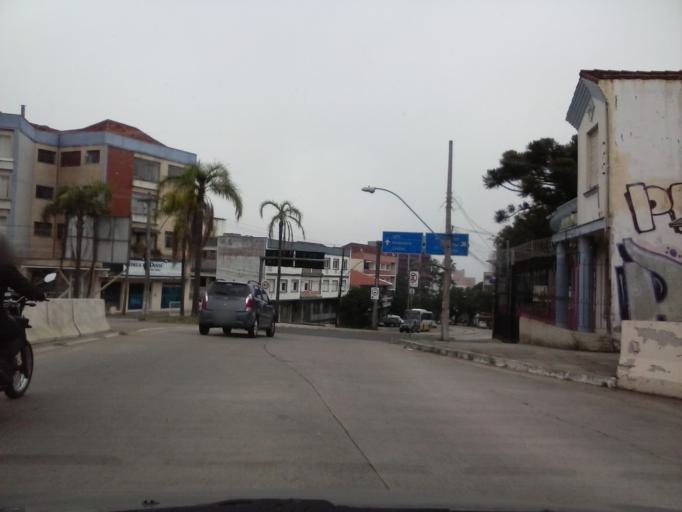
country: BR
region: Rio Grande do Sul
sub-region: Porto Alegre
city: Porto Alegre
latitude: -30.0383
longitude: -51.1741
